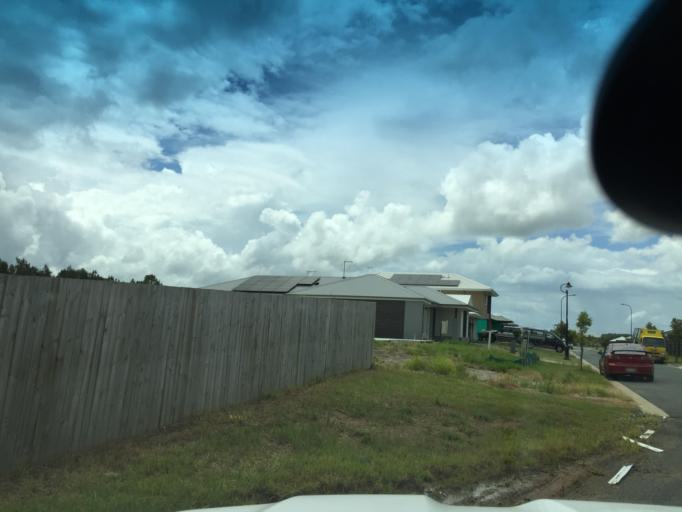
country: AU
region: Queensland
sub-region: Moreton Bay
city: Caboolture South
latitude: -27.0956
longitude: 152.9545
